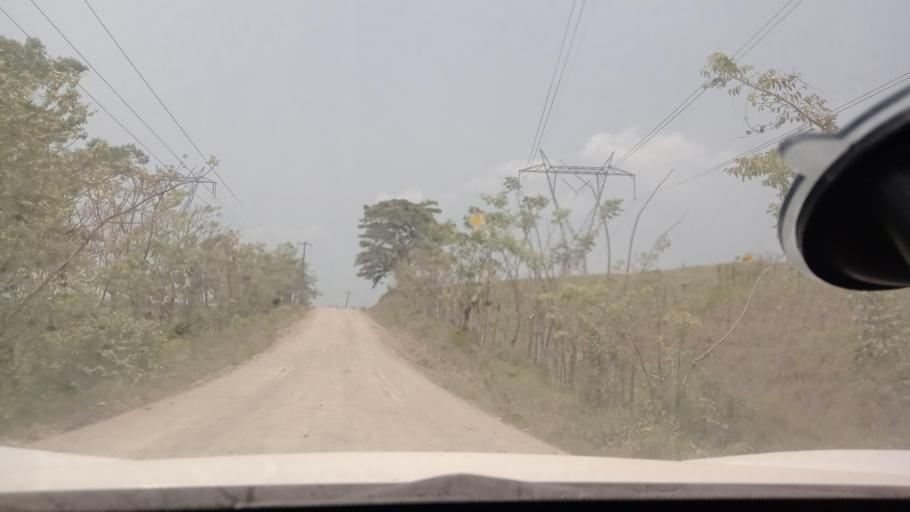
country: MX
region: Chiapas
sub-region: Tecpatan
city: Raudales Malpaso
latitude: 17.4439
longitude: -93.7884
